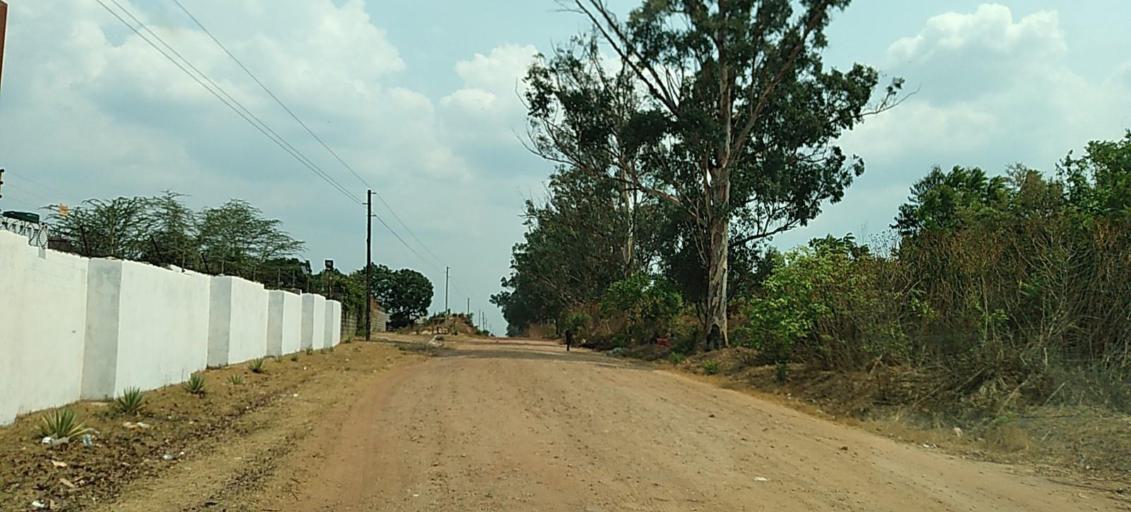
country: ZM
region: Copperbelt
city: Kalulushi
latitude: -12.8421
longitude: 28.0778
